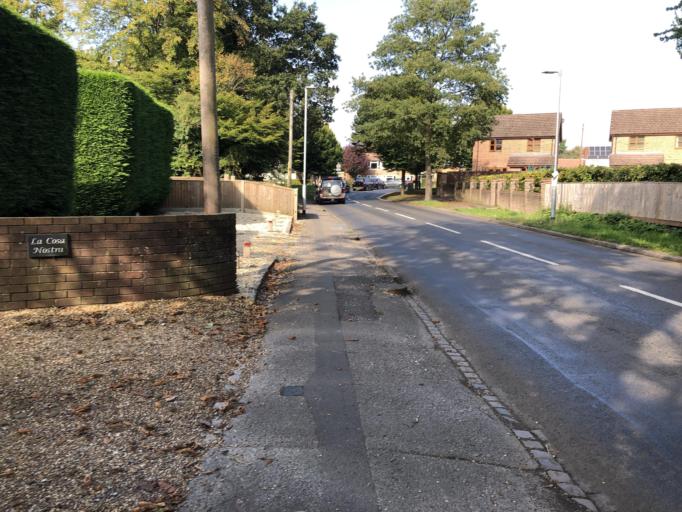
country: GB
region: England
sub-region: West Berkshire
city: Tilehurst
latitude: 51.4520
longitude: -1.0331
